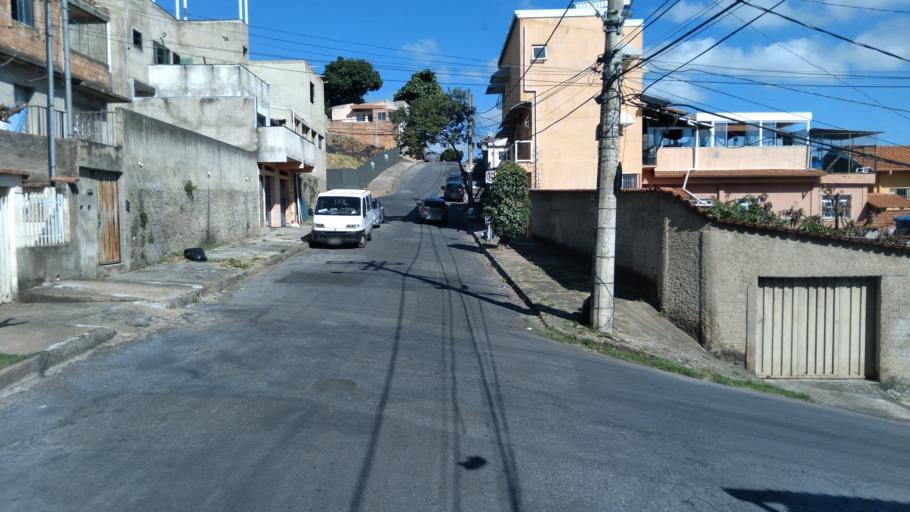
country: BR
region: Minas Gerais
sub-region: Belo Horizonte
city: Belo Horizonte
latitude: -19.8816
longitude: -43.9186
